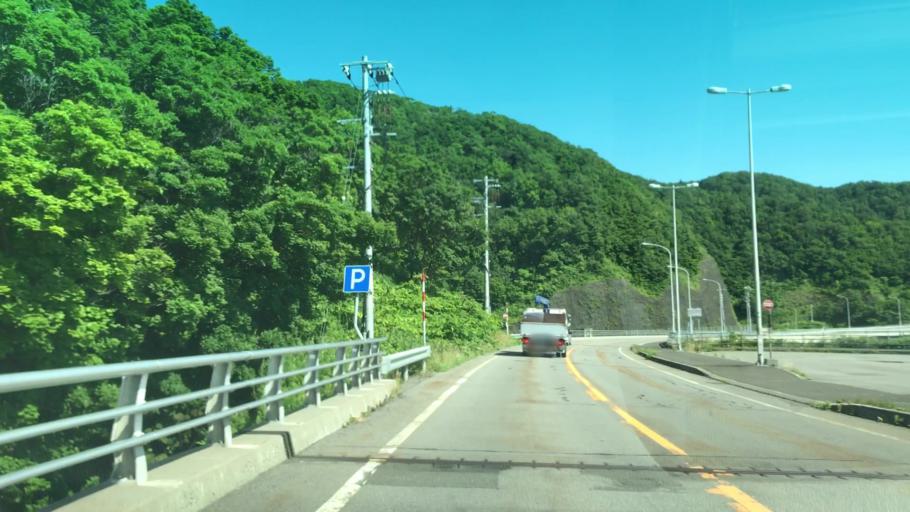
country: JP
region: Hokkaido
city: Iwanai
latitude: 43.1283
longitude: 140.4407
